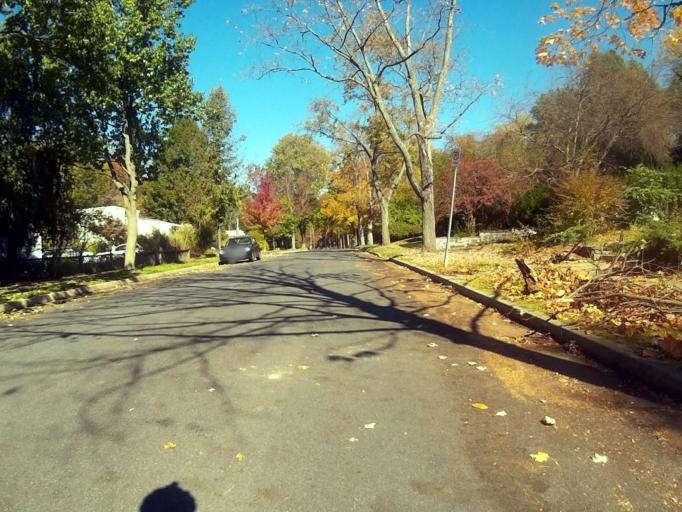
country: US
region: Pennsylvania
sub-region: Centre County
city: State College
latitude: 40.7956
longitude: -77.8817
